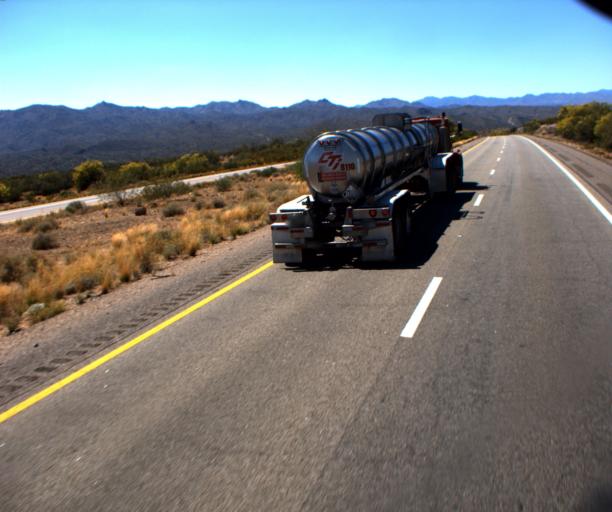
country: US
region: Arizona
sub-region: Yavapai County
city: Bagdad
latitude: 34.6282
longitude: -113.5396
